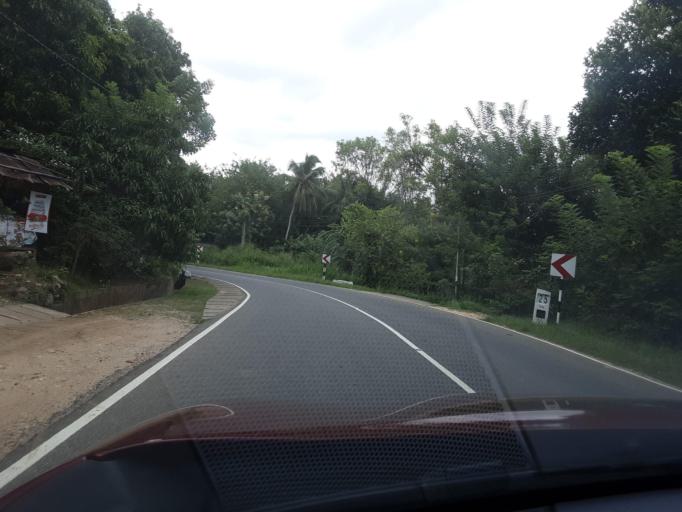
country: LK
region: Uva
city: Monaragala
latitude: 6.8941
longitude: 81.2909
